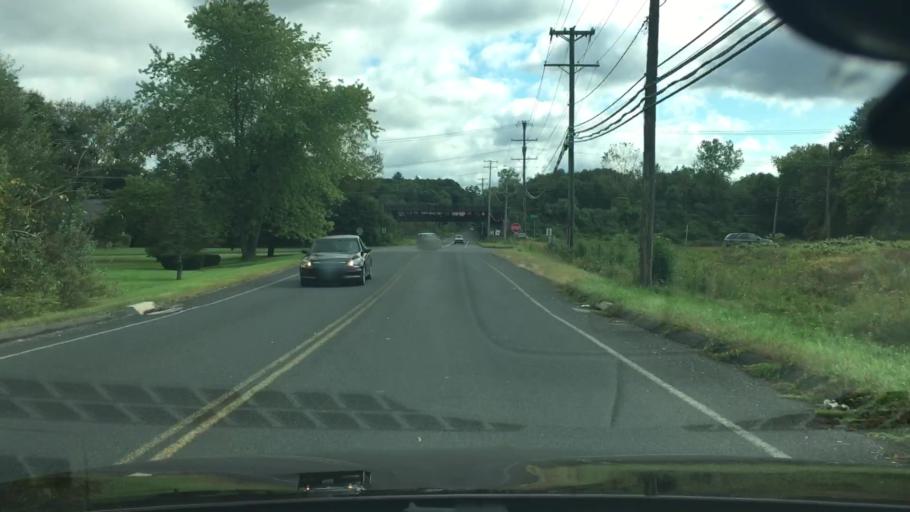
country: US
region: Connecticut
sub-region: New Haven County
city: Cheshire Village
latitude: 41.5558
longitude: -72.9045
